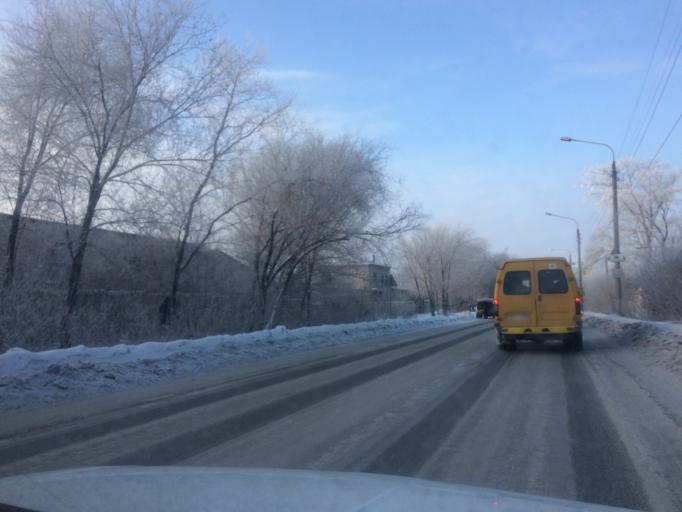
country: RU
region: Chelyabinsk
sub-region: Gorod Magnitogorsk
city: Magnitogorsk
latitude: 53.3952
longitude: 59.0731
